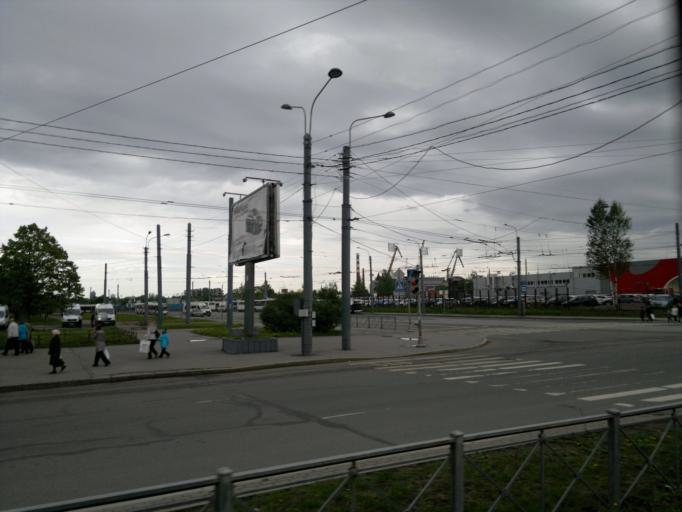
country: RU
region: St.-Petersburg
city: Vasyl'evsky Ostrov
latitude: 59.9554
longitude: 30.2351
